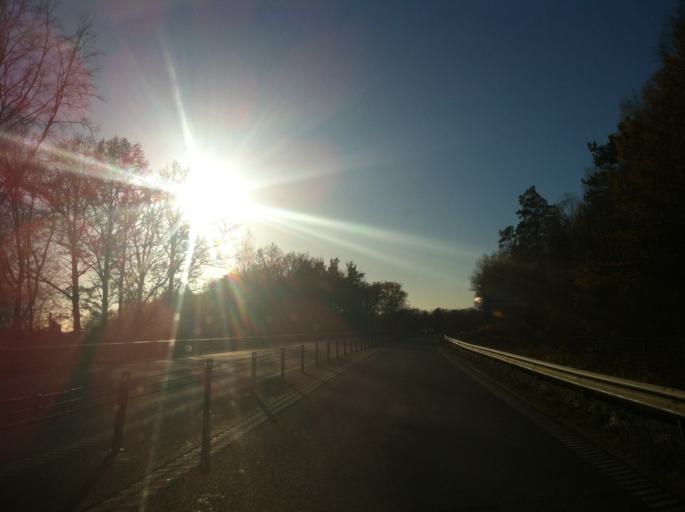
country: SE
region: Blekinge
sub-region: Karlshamns Kommun
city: Morrum
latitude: 56.1860
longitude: 14.7818
